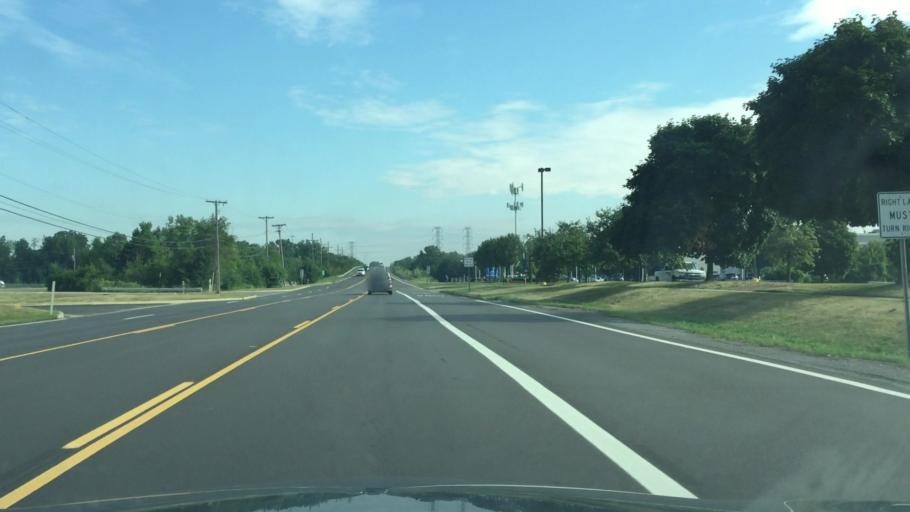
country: US
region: Michigan
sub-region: Oakland County
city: Novi
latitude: 42.4747
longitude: -83.4346
